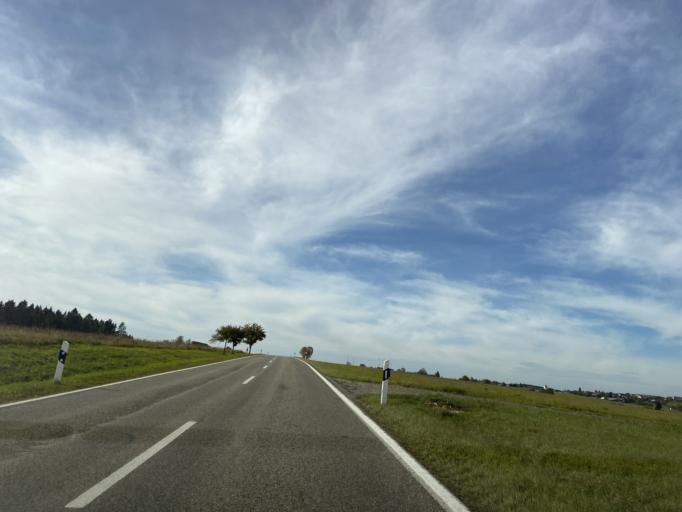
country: DE
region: Baden-Wuerttemberg
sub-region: Tuebingen Region
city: Leibertingen
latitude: 48.0542
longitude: 9.0744
